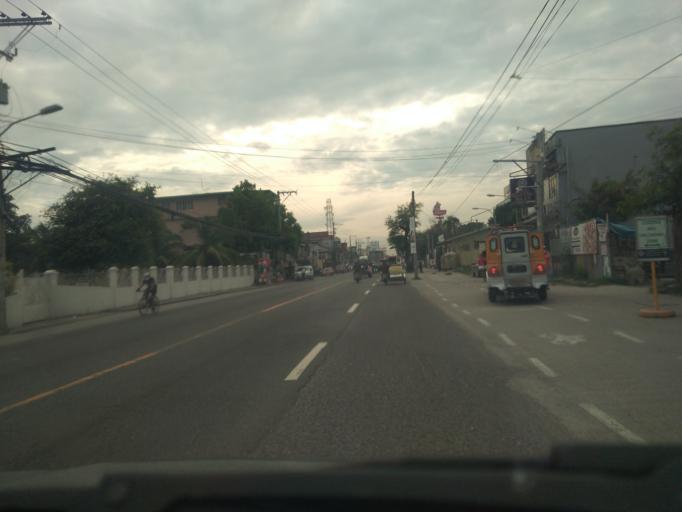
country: PH
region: Central Luzon
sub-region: Province of Pampanga
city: San Fernando
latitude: 15.0356
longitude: 120.6844
